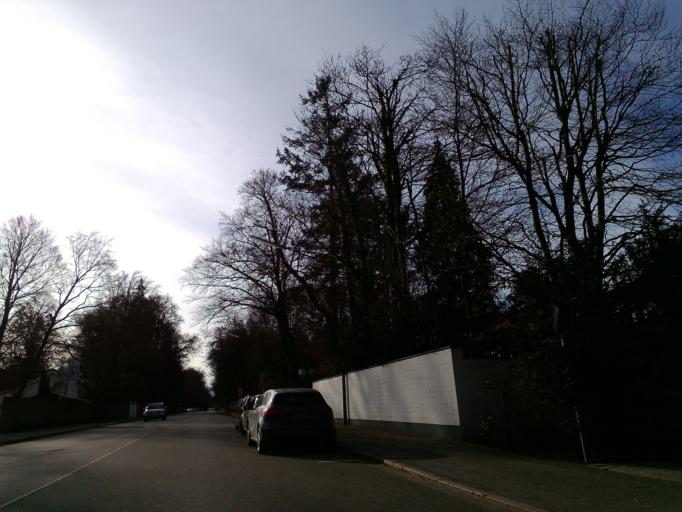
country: DE
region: Bavaria
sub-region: Upper Bavaria
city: Pullach im Isartal
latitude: 48.0572
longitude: 11.5400
